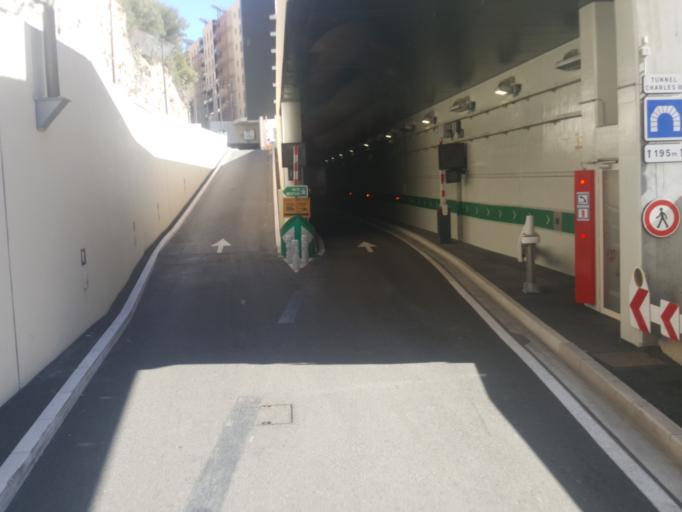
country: MC
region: Commune de Monaco
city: Monaco
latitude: 43.7307
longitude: 7.4147
